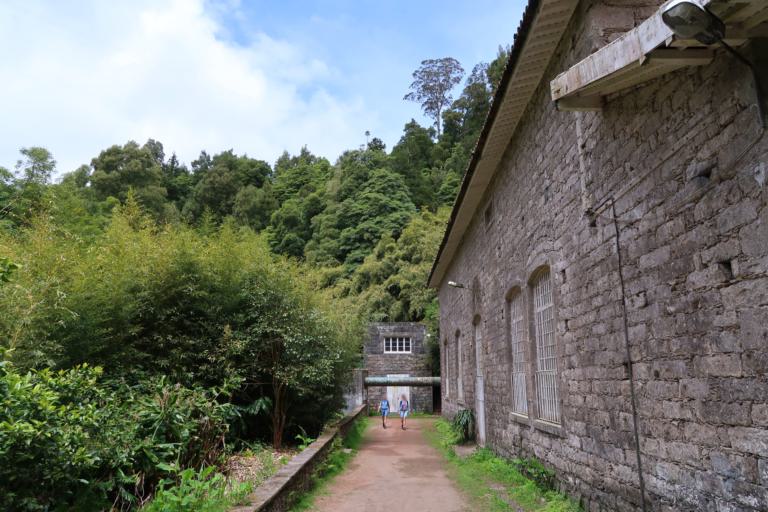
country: PT
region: Azores
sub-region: Ribeira Grande
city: Rabo de Peixe
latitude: 37.7951
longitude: -25.4921
